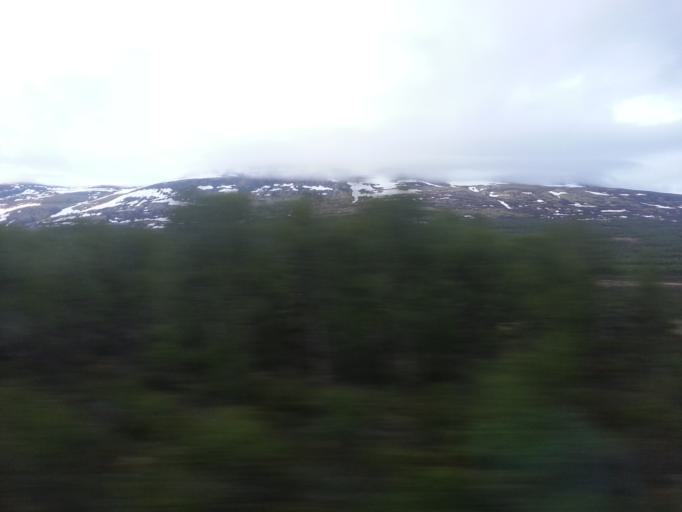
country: NO
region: Oppland
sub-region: Dovre
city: Dovre
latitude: 62.1509
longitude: 9.3216
